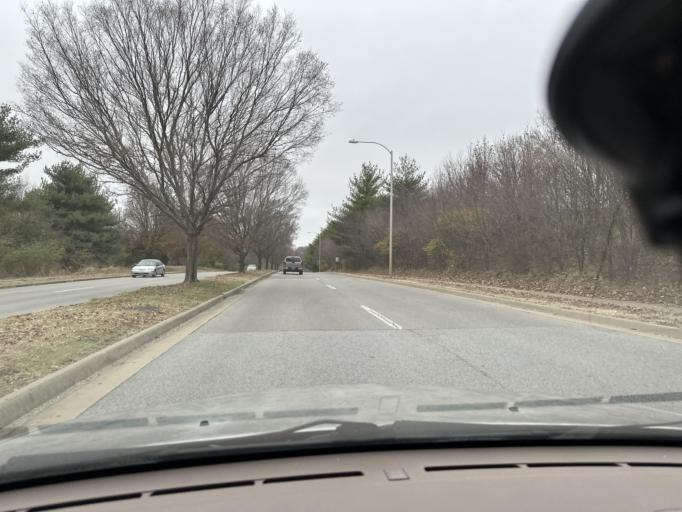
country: US
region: Arkansas
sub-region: Washington County
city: Johnson
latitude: 36.1253
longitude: -94.1580
